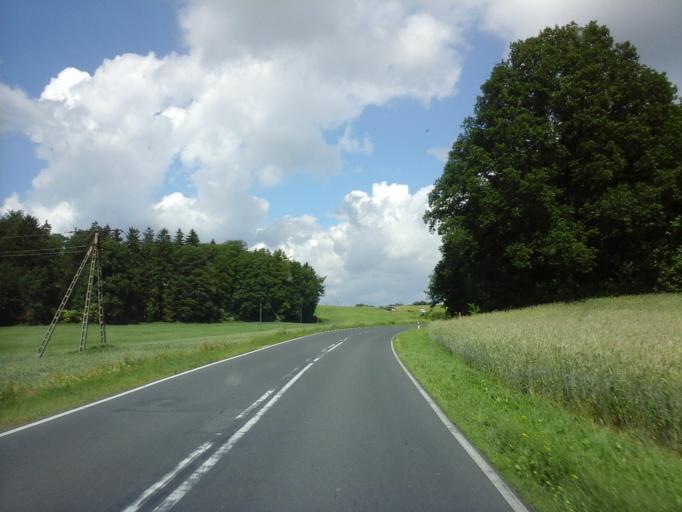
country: PL
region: West Pomeranian Voivodeship
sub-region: Powiat swidwinski
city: Swidwin
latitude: 53.8046
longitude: 15.7716
